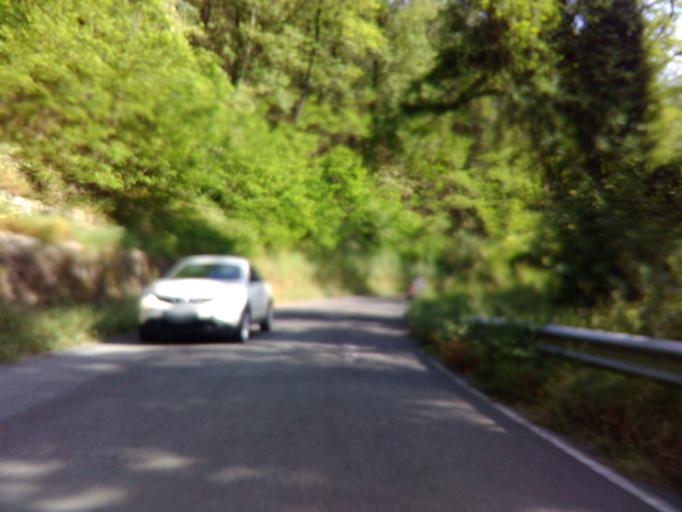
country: IT
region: Tuscany
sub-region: Provincia di Massa-Carrara
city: Fosdinovo
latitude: 44.1178
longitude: 10.0649
